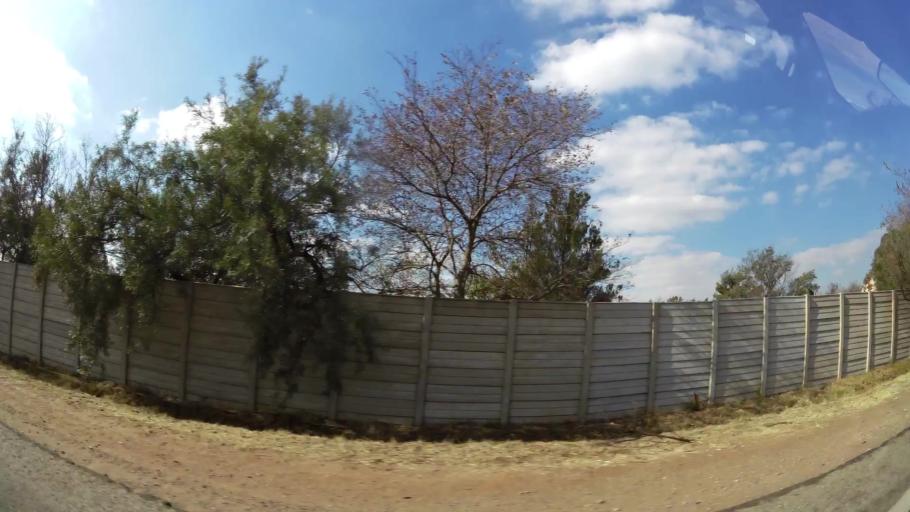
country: ZA
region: Gauteng
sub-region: West Rand District Municipality
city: Krugersdorp
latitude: -26.0633
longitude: 27.7603
